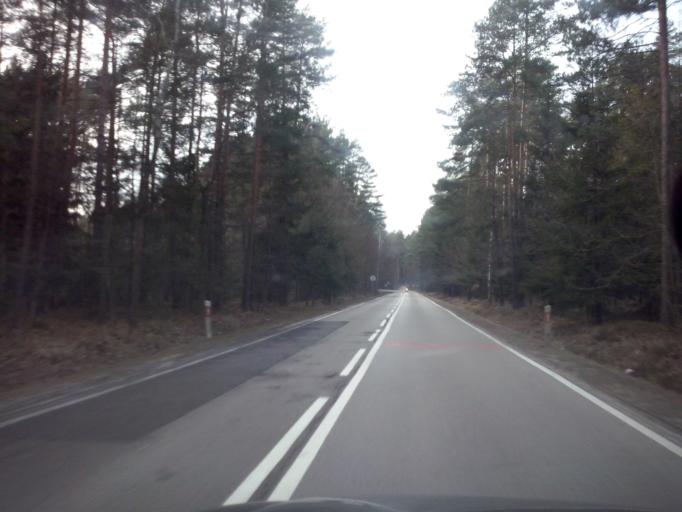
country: PL
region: Subcarpathian Voivodeship
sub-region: Powiat nizanski
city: Harasiuki
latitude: 50.5073
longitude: 22.5679
